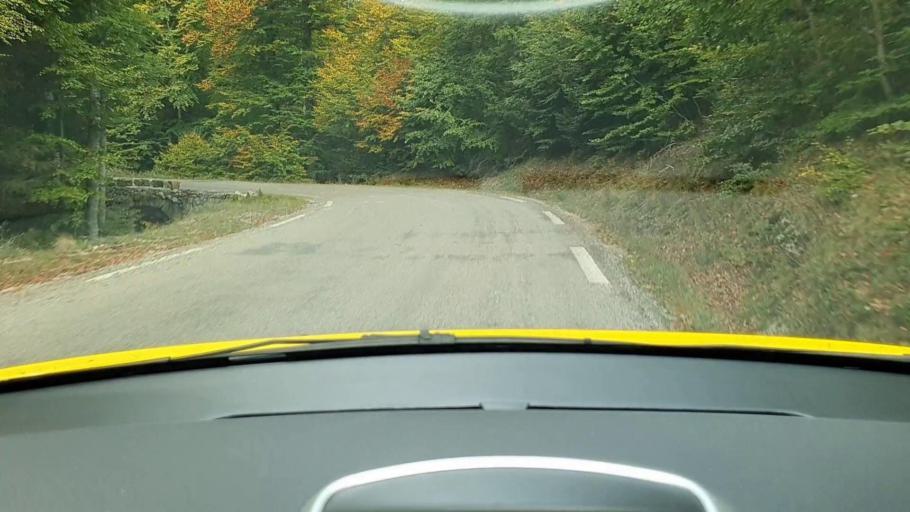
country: FR
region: Languedoc-Roussillon
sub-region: Departement du Gard
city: Le Vigan
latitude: 44.0539
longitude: 3.5506
